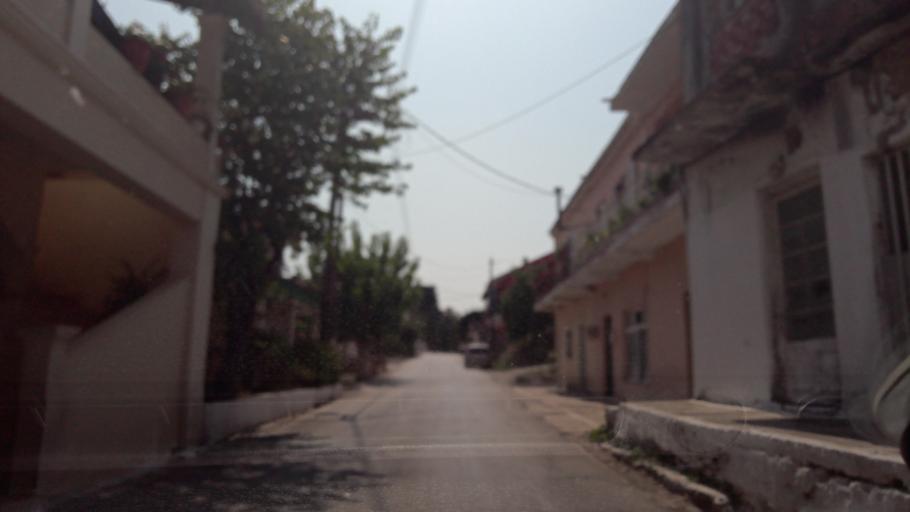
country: GR
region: Ionian Islands
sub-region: Nomos Kerkyras
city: Perivoli
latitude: 39.4104
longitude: 20.0224
